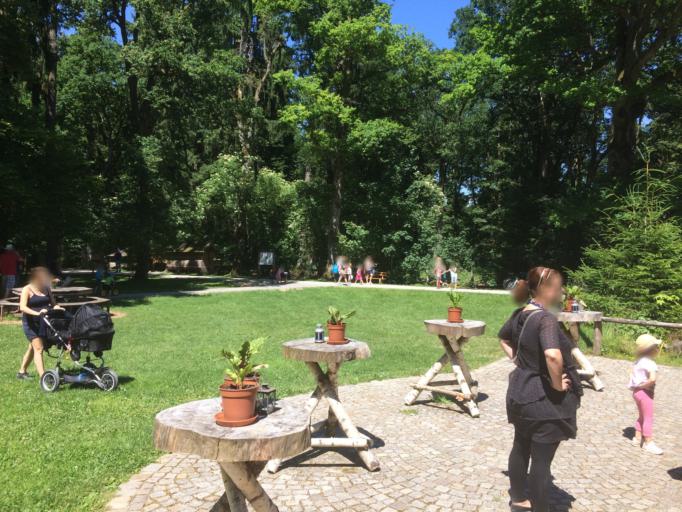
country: DE
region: Bavaria
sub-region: Upper Bavaria
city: Grunwald
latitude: 48.0253
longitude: 11.5256
